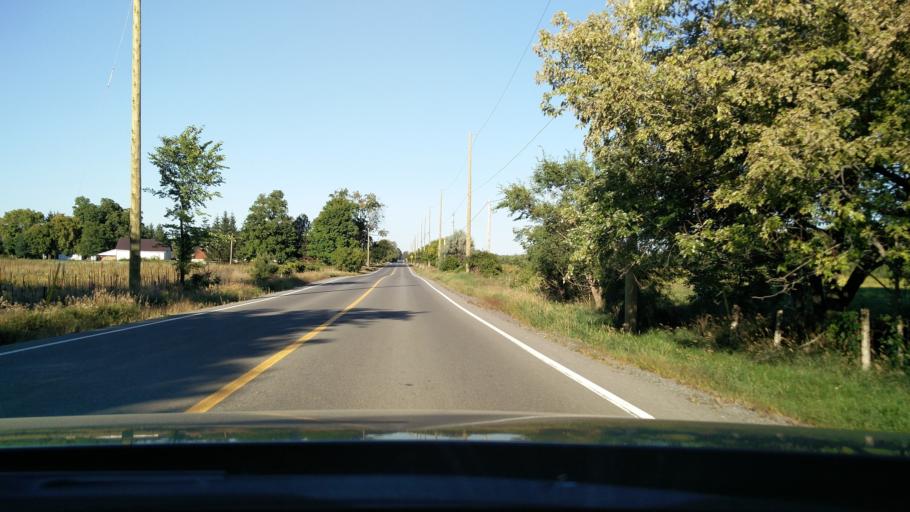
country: CA
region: Ontario
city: Bells Corners
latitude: 45.2326
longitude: -75.7333
